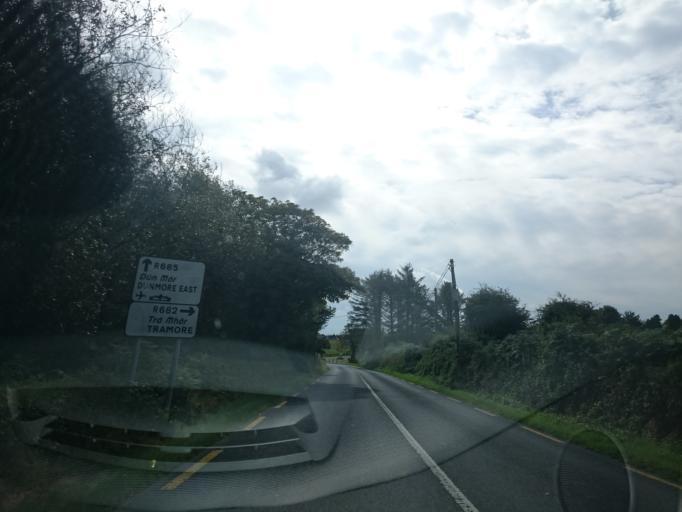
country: IE
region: Munster
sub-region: Waterford
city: Tra Mhor
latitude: 52.1809
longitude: -7.1703
